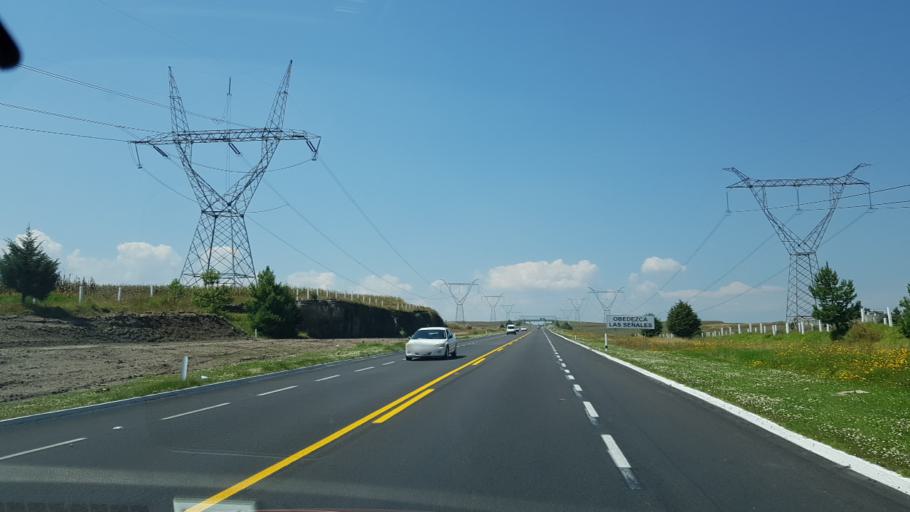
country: MX
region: Mexico
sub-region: Almoloya de Juarez
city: Conjunto Habitacional Ecologico SUTEYM
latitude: 19.3844
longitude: -99.7722
